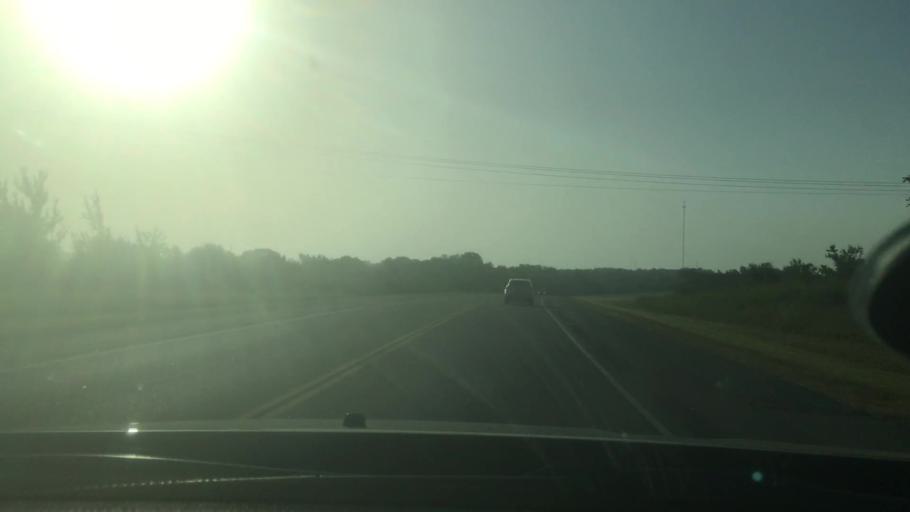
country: US
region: Oklahoma
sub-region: Pontotoc County
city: Ada
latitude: 34.6424
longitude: -96.4930
